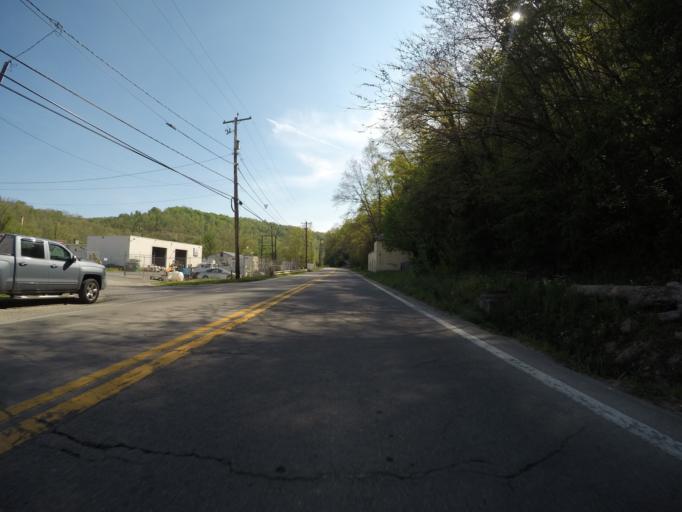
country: US
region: West Virginia
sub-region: Kanawha County
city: Clendenin
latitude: 38.4686
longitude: -81.4020
